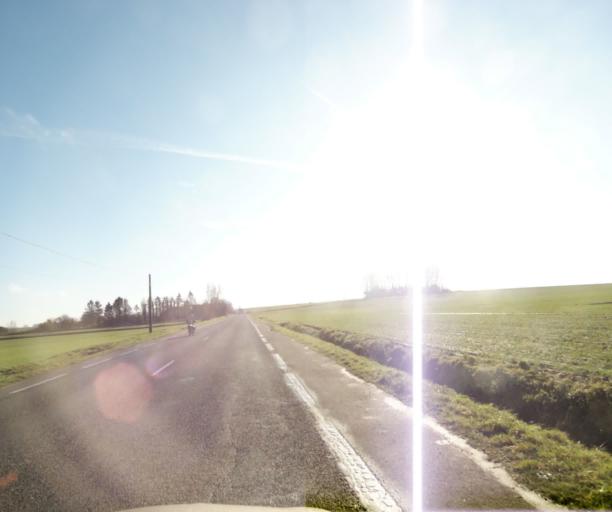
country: FR
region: Nord-Pas-de-Calais
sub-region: Departement du Nord
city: Preseau
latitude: 50.3240
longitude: 3.5632
